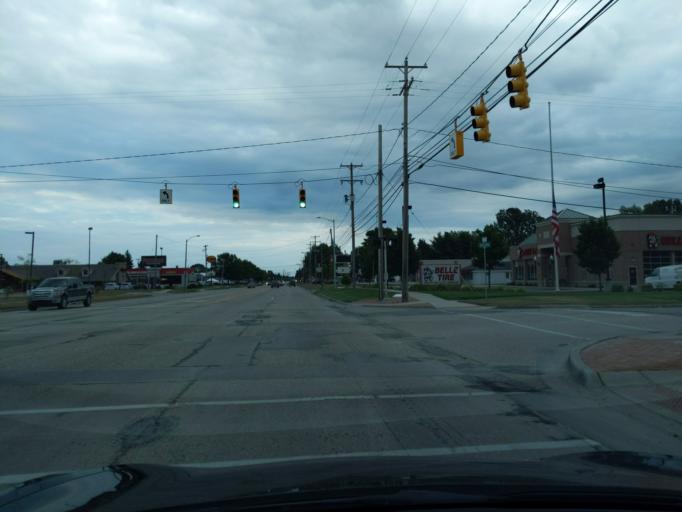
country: US
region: Michigan
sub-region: Isabella County
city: Mount Pleasant
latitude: 43.6117
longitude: -84.7633
